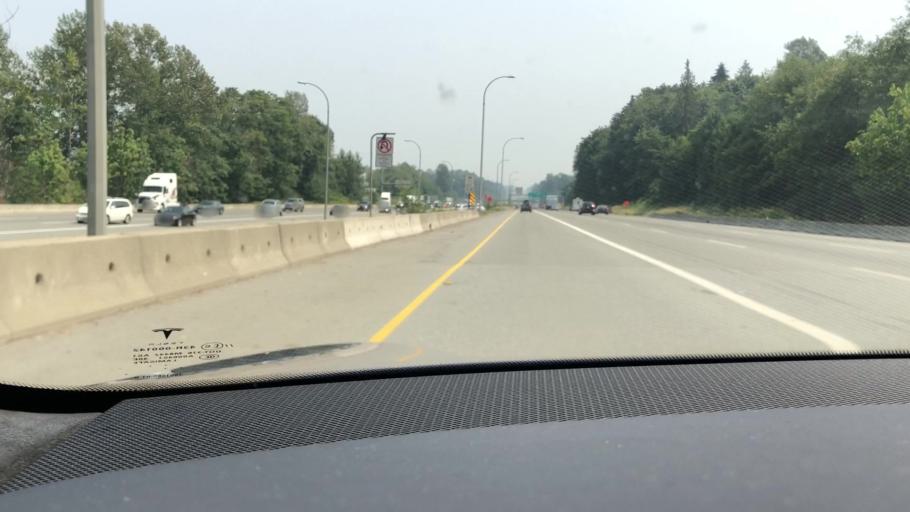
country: CA
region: British Columbia
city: Pitt Meadows
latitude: 49.1732
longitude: -122.7037
